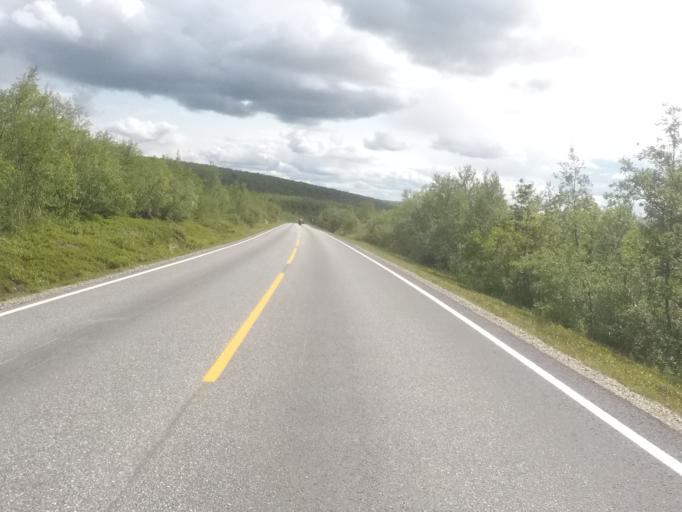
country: NO
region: Finnmark Fylke
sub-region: Karasjok
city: Karasjohka
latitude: 69.5120
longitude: 25.4661
